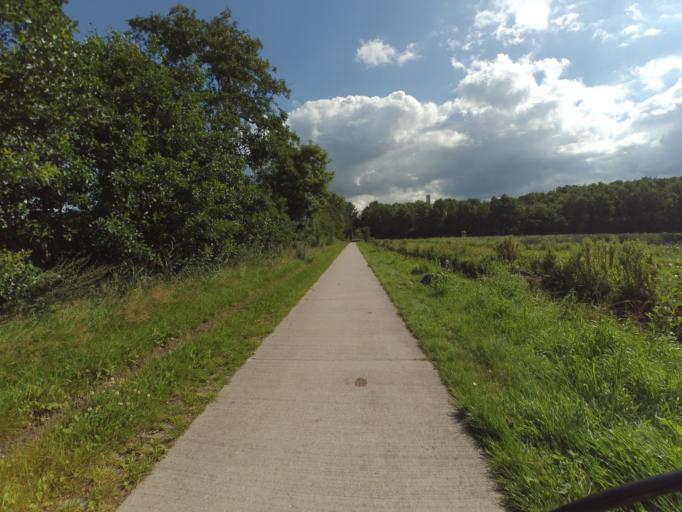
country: NL
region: Friesland
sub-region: Gemeente Tytsjerksteradiel
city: Noardburgum
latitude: 53.2085
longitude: 6.0225
